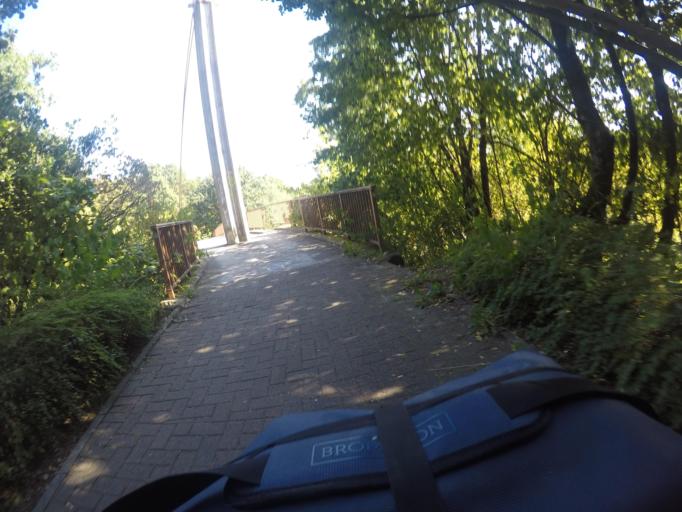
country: DE
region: Hesse
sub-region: Regierungsbezirk Darmstadt
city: Kriftel
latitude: 50.0787
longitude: 8.4628
